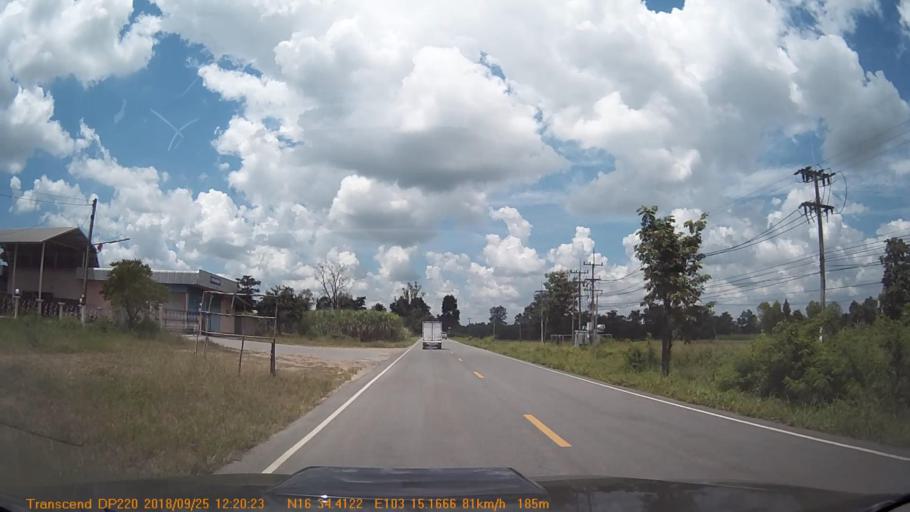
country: TH
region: Kalasin
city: Huai Mek
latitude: 16.5735
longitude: 103.2530
